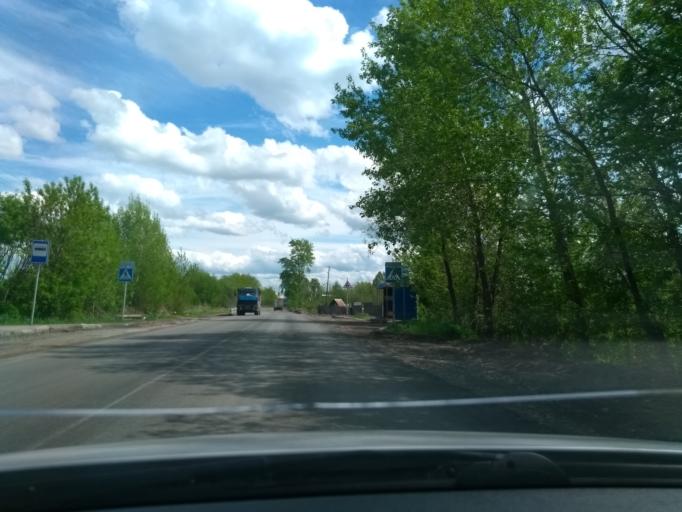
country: RU
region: Perm
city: Kondratovo
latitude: 58.0093
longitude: 56.0815
